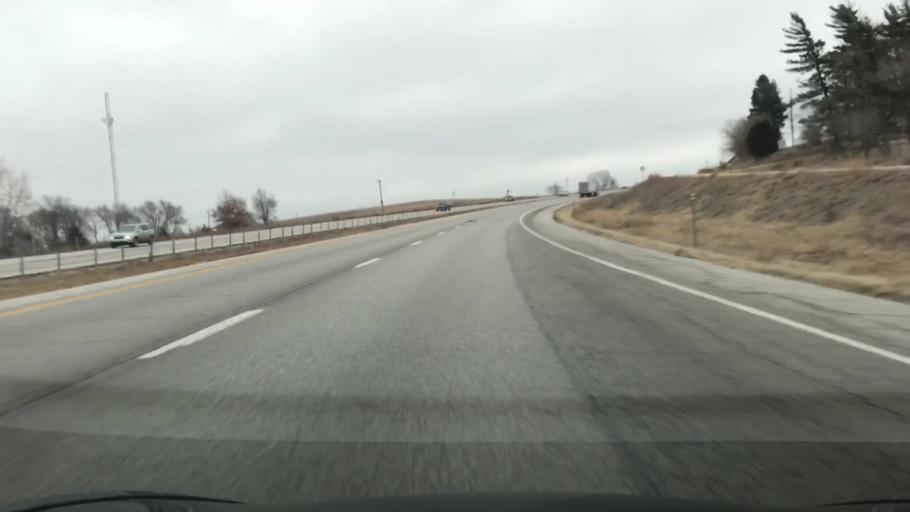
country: US
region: Iowa
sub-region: Madison County
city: Earlham
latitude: 41.5164
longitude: -94.1921
